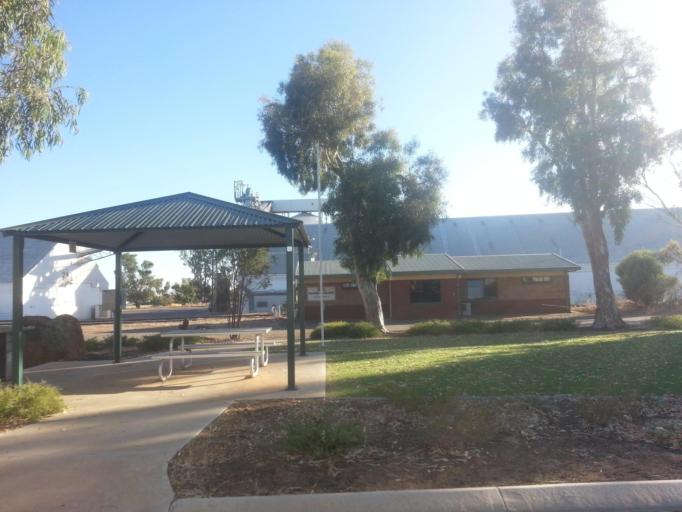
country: AU
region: Western Australia
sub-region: Wongan-Ballidu
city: Wongan Hills
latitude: -30.3614
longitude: 117.1164
